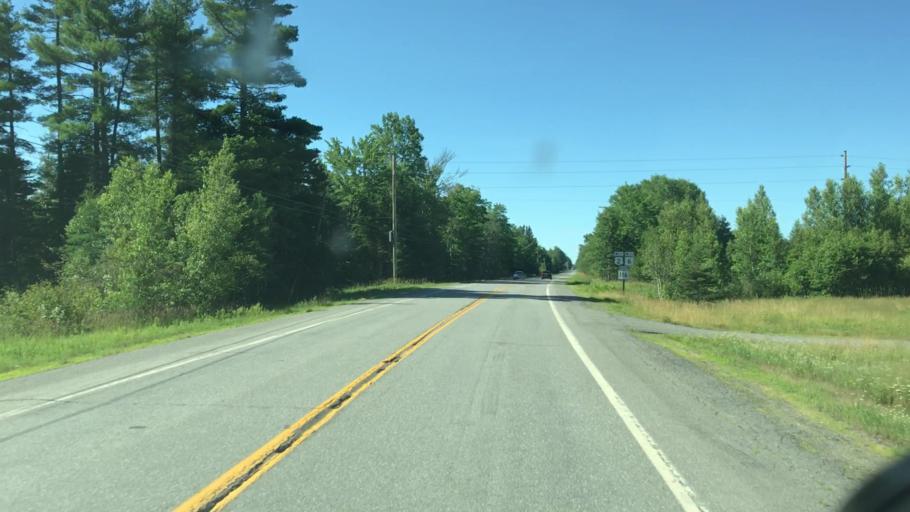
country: US
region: Maine
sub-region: Penobscot County
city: Howland
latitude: 45.2515
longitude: -68.6379
